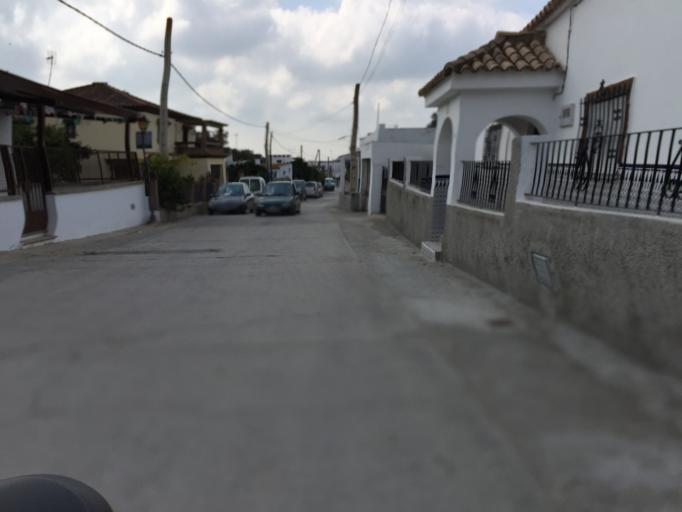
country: ES
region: Andalusia
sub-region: Provincia de Cadiz
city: Benalup-Casas Viejas
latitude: 36.3177
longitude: -5.8847
